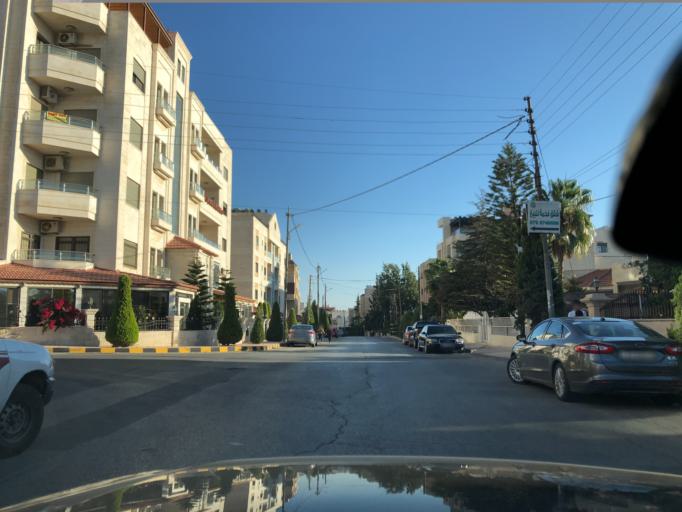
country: JO
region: Amman
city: Wadi as Sir
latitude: 31.9518
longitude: 35.8570
